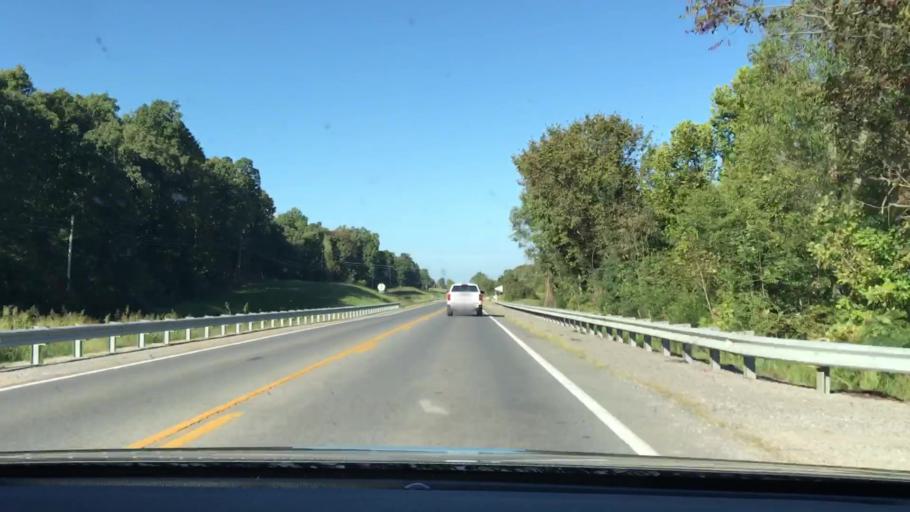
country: US
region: Kentucky
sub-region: Marshall County
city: Calvert City
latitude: 37.0046
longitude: -88.3742
